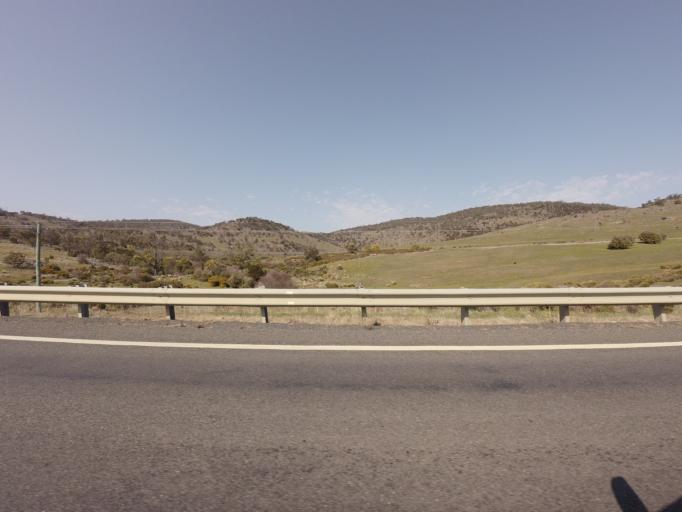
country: AU
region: Tasmania
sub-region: Northern Midlands
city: Evandale
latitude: -41.8149
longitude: 147.5793
